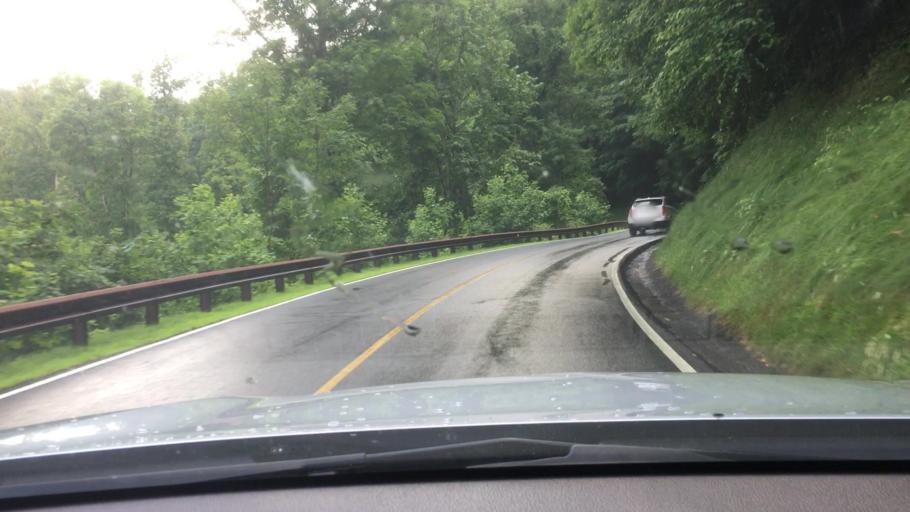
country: US
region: North Carolina
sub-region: Yancey County
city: Burnsville
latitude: 35.8821
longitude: -82.3506
